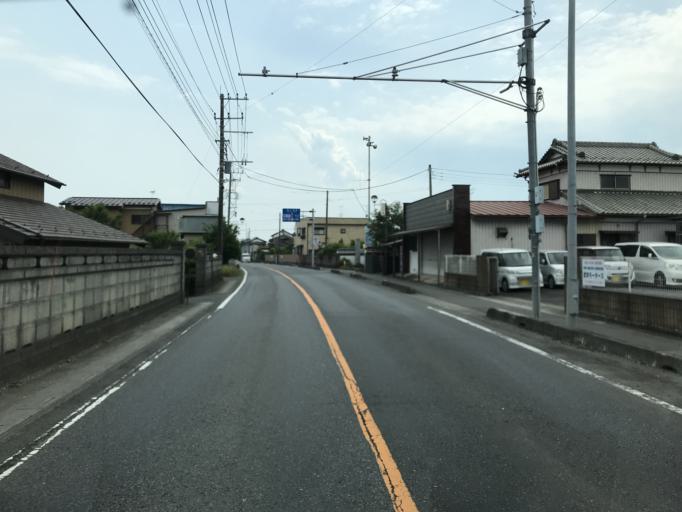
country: JP
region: Saitama
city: Kukichuo
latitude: 36.0843
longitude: 139.6491
